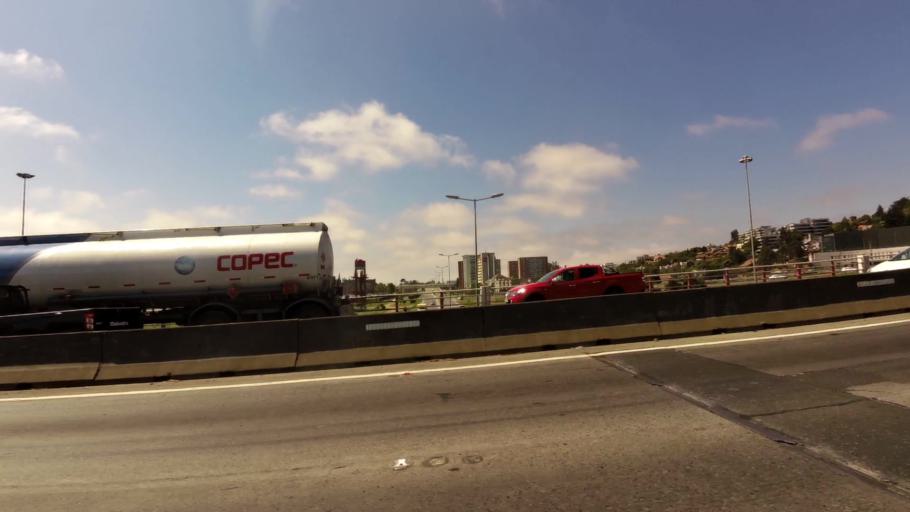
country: CL
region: Biobio
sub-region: Provincia de Concepcion
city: Concepcion
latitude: -36.7956
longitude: -73.0662
